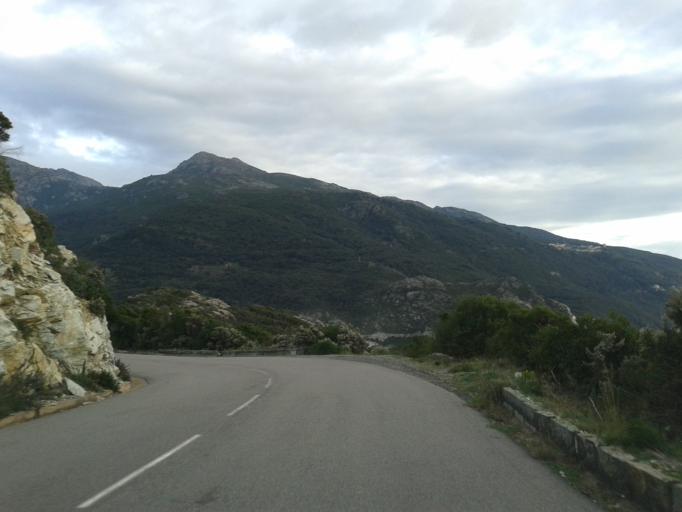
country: FR
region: Corsica
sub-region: Departement de la Haute-Corse
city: Brando
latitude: 42.8717
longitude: 9.3368
